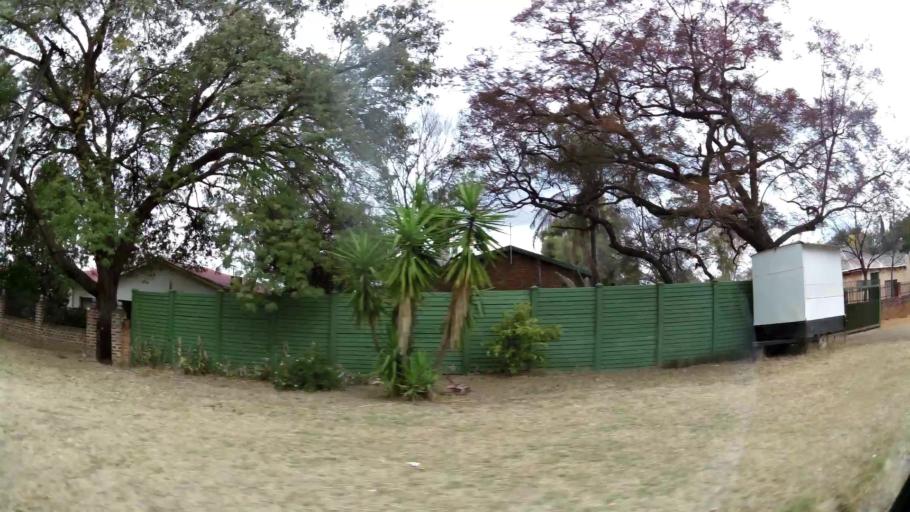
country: ZA
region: Limpopo
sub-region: Waterberg District Municipality
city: Modimolle
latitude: -24.7004
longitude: 28.4131
